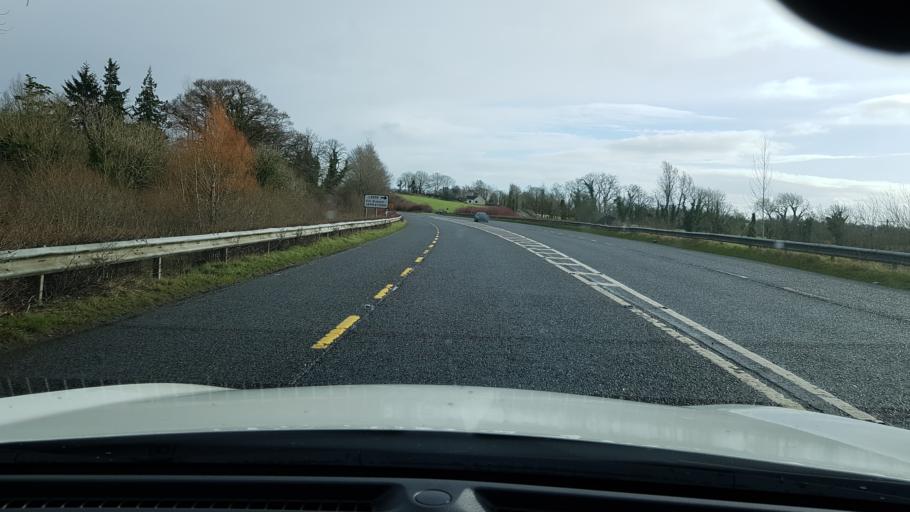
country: IE
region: Connaught
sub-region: County Leitrim
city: Carrick-on-Shannon
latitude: 53.9343
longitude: -8.0472
